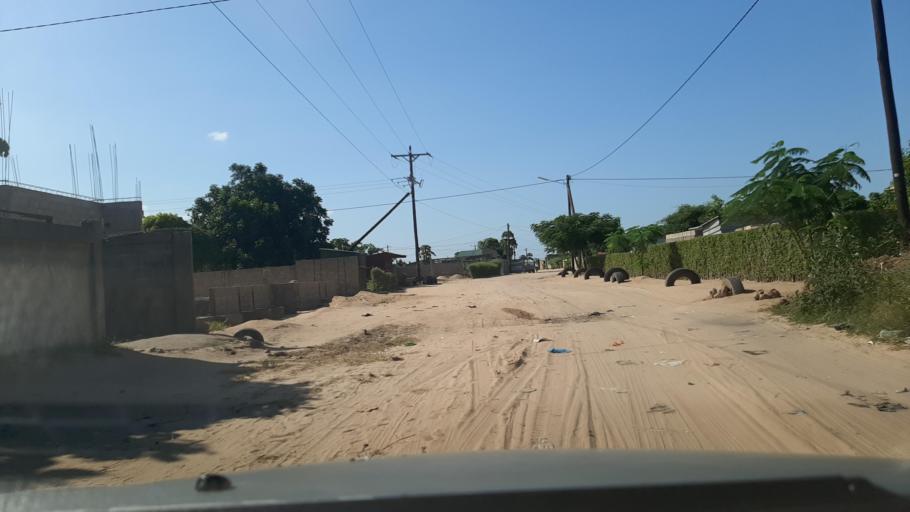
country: MZ
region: Maputo
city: Matola
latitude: -25.8106
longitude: 32.4917
